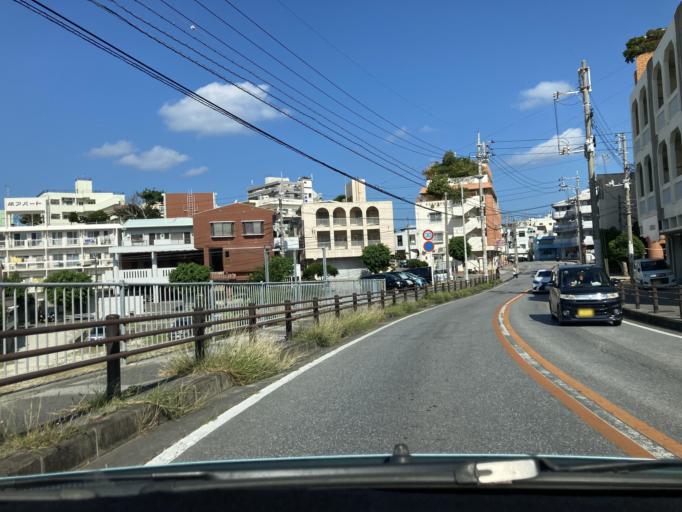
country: JP
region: Okinawa
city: Tomigusuku
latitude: 26.1837
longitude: 127.6609
